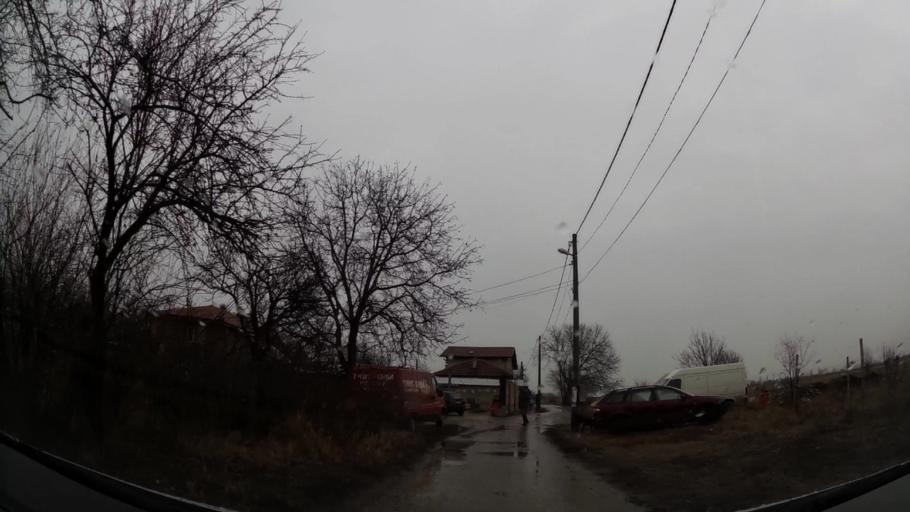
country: BG
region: Sofia-Capital
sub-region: Stolichna Obshtina
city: Sofia
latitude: 42.6582
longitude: 23.4287
